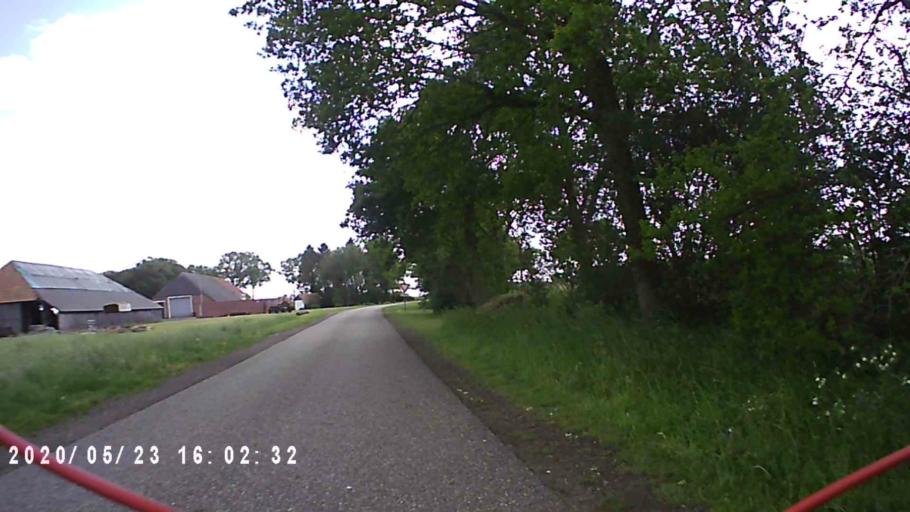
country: NL
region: Groningen
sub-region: Gemeente Delfzijl
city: Delfzijl
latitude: 53.2459
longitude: 6.8996
